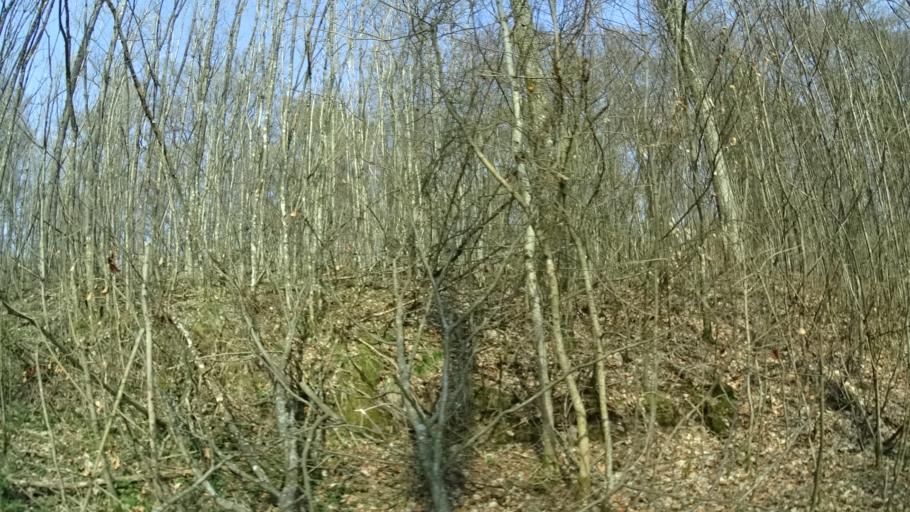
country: DE
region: Rheinland-Pfalz
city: Thallichtenberg
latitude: 49.5872
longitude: 7.3534
